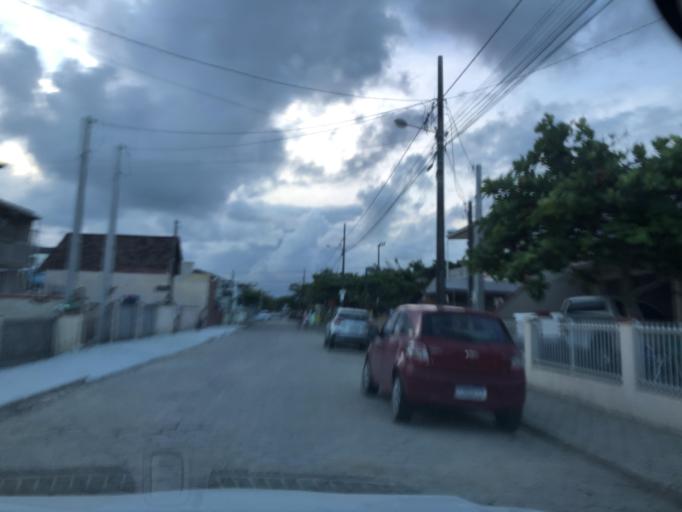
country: BR
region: Santa Catarina
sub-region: Sao Francisco Do Sul
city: Sao Francisco do Sul
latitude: -26.2333
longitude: -48.5049
